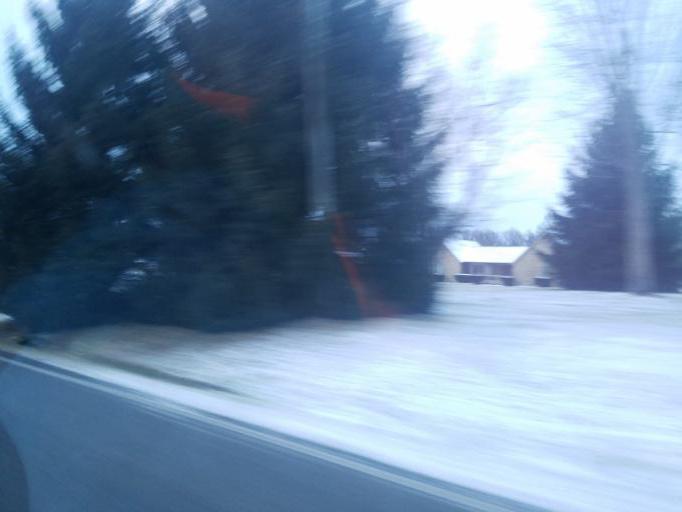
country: US
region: Ohio
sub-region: Delaware County
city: Sunbury
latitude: 40.1678
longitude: -82.8533
